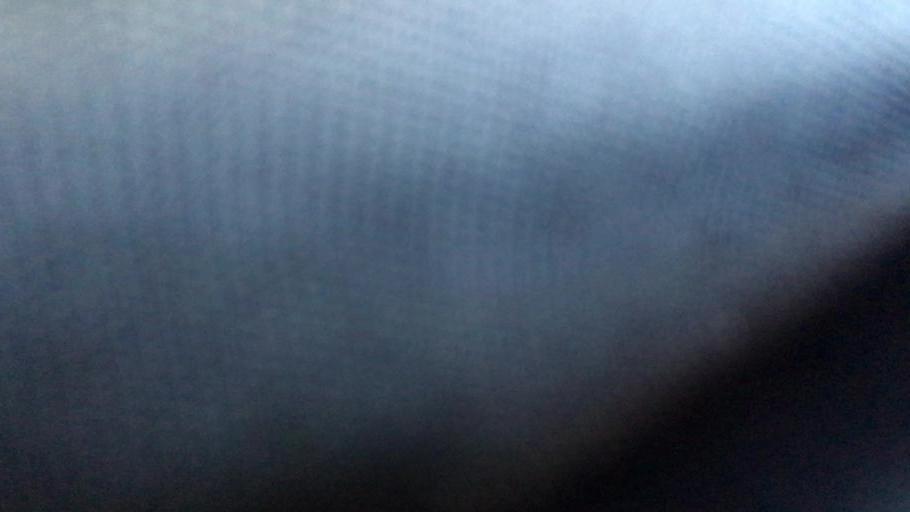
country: US
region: Maryland
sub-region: Somerset County
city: Princess Anne
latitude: 38.1318
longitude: -75.6980
